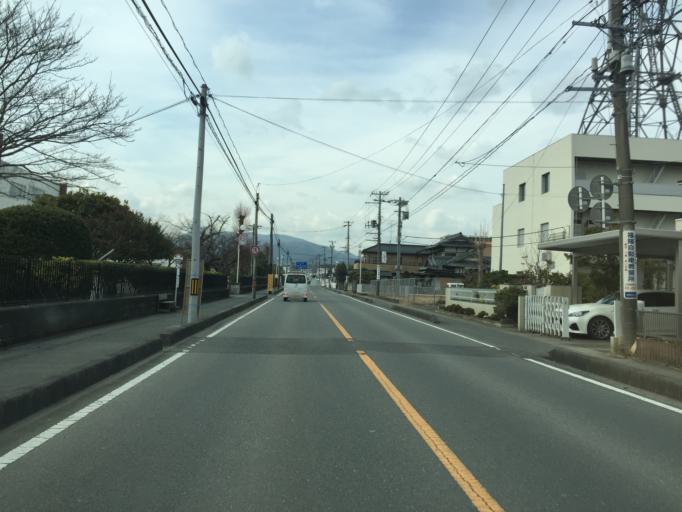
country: JP
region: Ibaraki
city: Kitaibaraki
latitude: 36.8891
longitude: 140.7687
